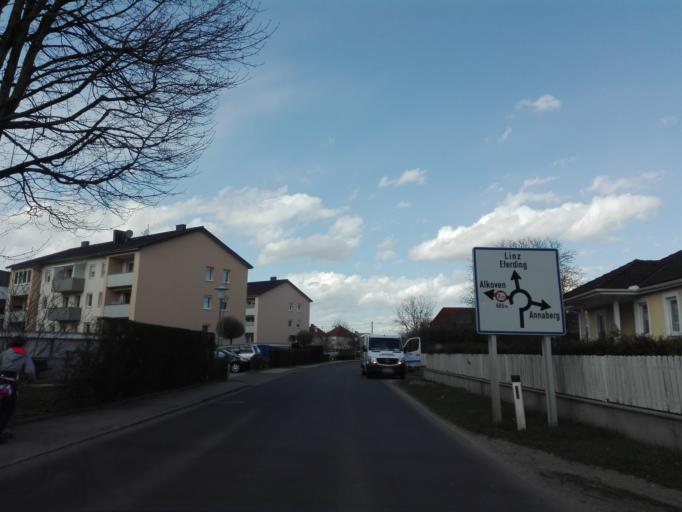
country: AT
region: Upper Austria
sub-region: Politischer Bezirk Urfahr-Umgebung
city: Goldworth
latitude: 48.2813
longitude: 14.1112
